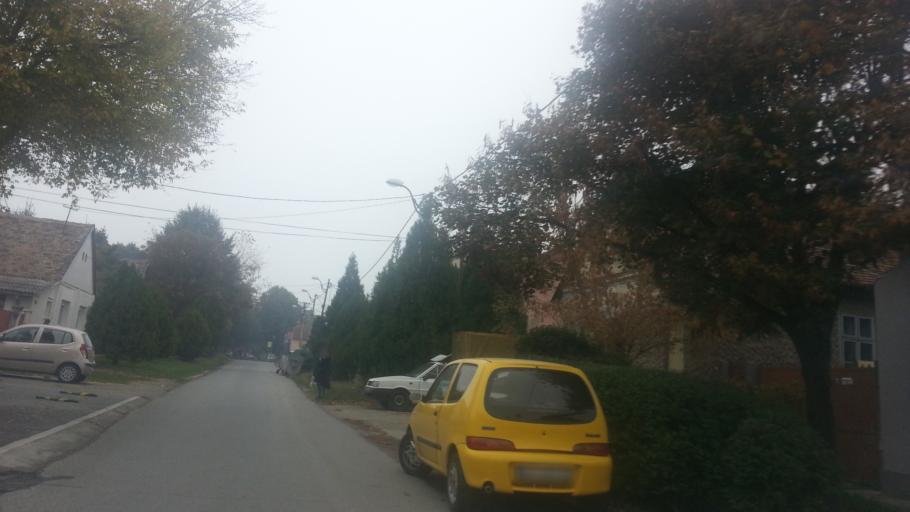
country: RS
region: Central Serbia
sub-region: Belgrade
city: Zemun
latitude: 44.8487
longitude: 20.3878
